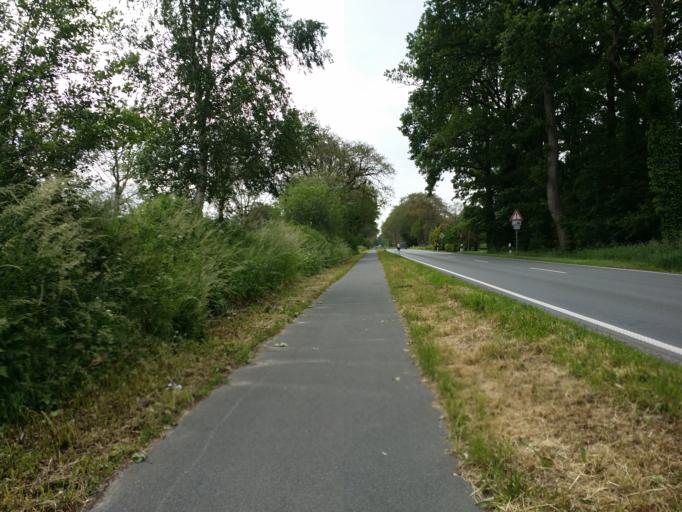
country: DE
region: Lower Saxony
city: Wittmund
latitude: 53.5399
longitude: 7.7820
